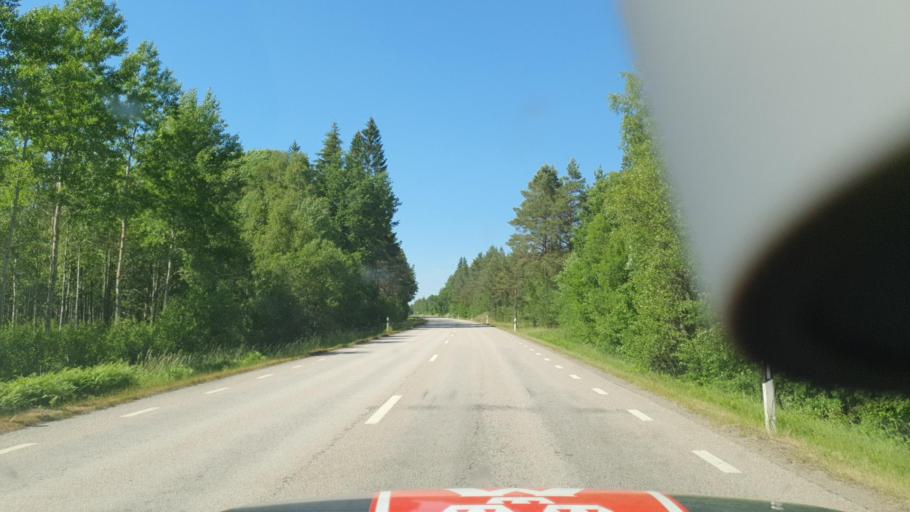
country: SE
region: Kalmar
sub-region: Emmaboda Kommun
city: Emmaboda
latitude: 56.5504
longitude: 15.6103
